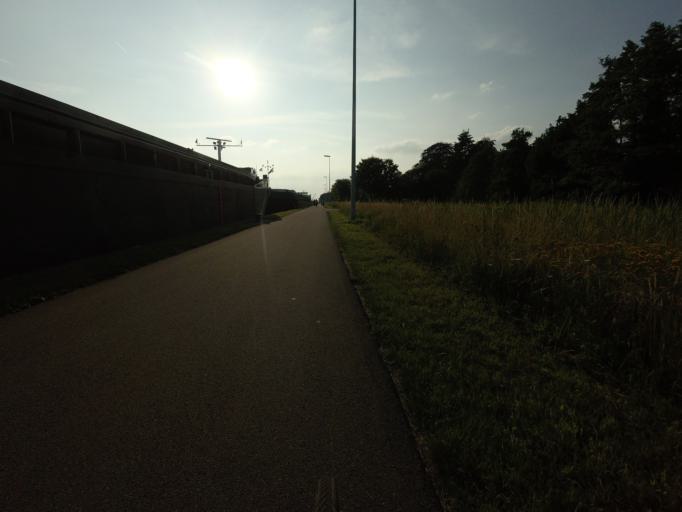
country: BE
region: Flanders
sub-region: Provincie Antwerpen
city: Wijnegem
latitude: 51.2240
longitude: 4.5481
